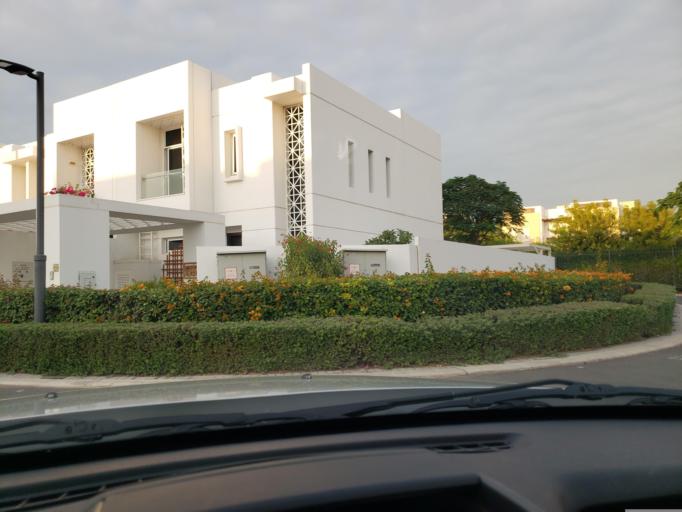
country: AE
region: Dubai
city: Dubai
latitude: 25.0193
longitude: 55.2743
